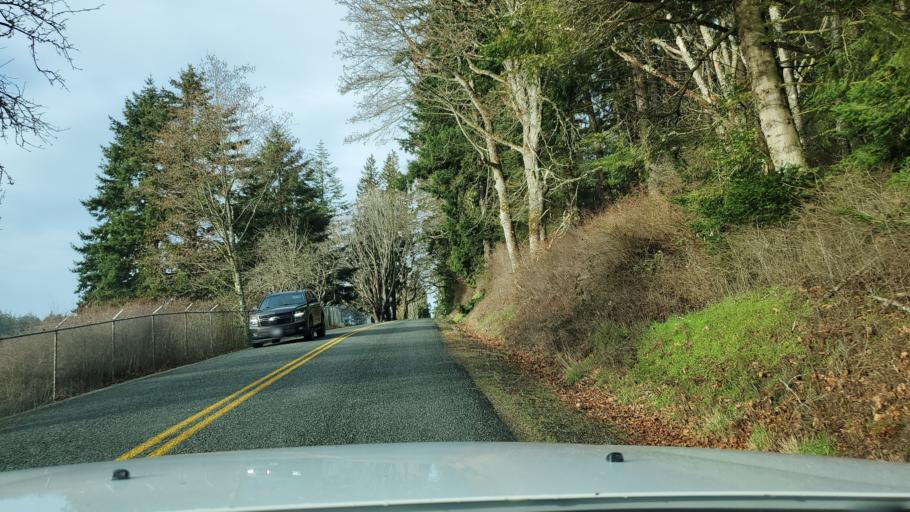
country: US
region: Washington
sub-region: Skagit County
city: Anacortes
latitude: 48.4535
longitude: -122.5751
